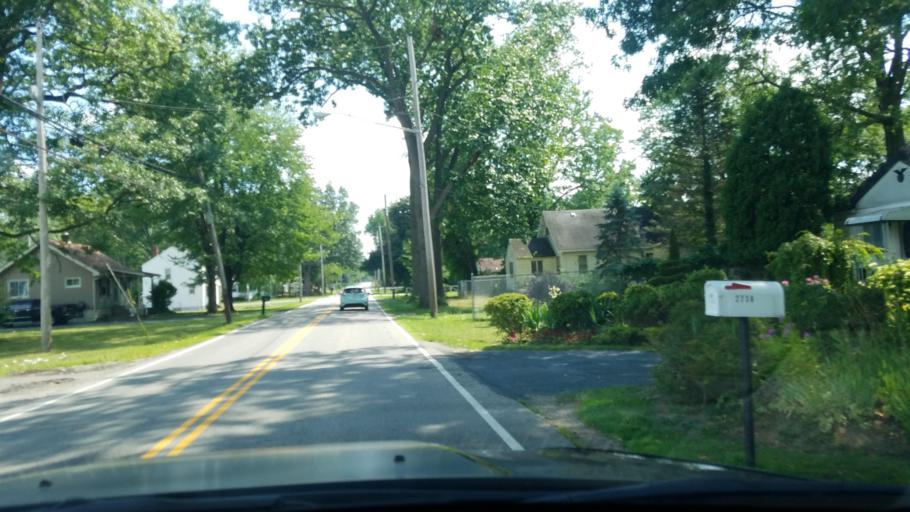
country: US
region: Ohio
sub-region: Trumbull County
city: Bolindale
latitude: 41.2148
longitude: -80.7816
